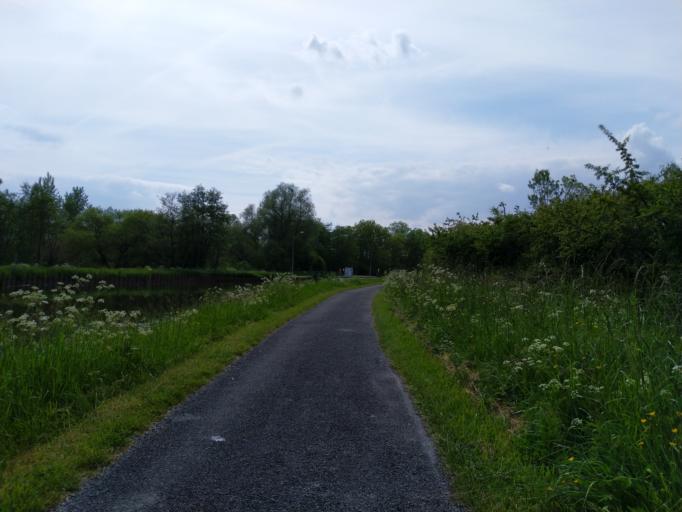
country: FR
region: Picardie
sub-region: Departement de l'Aisne
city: Boue
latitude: 49.9961
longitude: 3.6758
